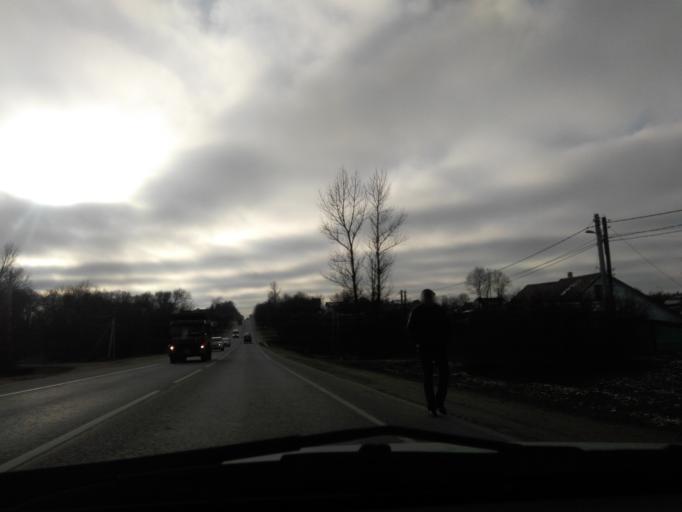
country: RU
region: Moskovskaya
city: Troitsk
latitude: 55.3039
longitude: 37.1419
